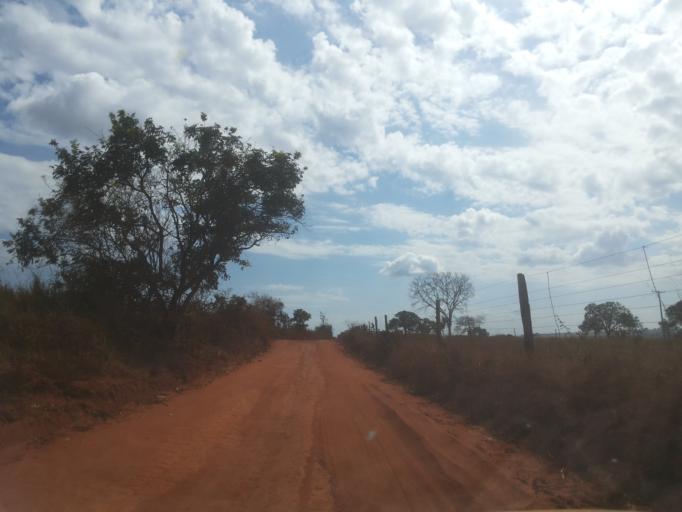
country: BR
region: Minas Gerais
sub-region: Ituiutaba
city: Ituiutaba
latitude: -19.0250
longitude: -49.3934
